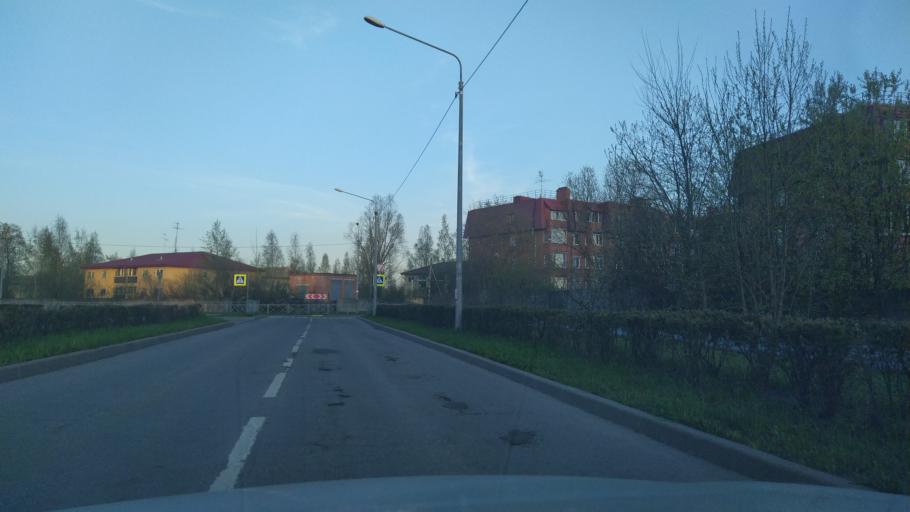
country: RU
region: St.-Petersburg
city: Pushkin
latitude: 59.7019
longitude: 30.3810
